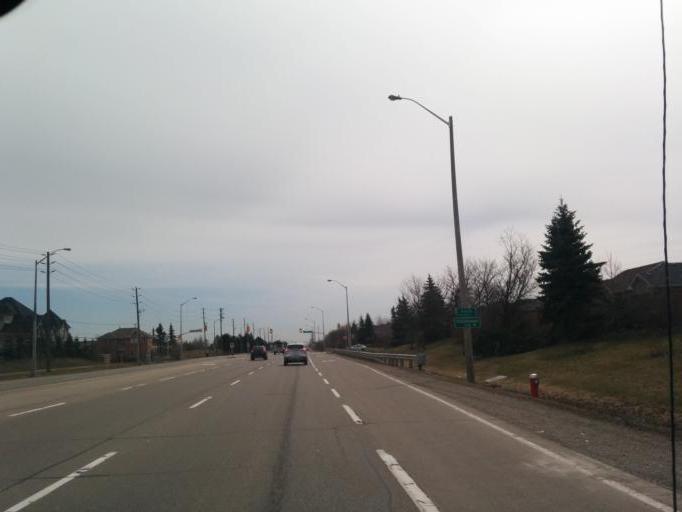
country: CA
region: Ontario
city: Brampton
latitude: 43.7290
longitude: -79.8186
